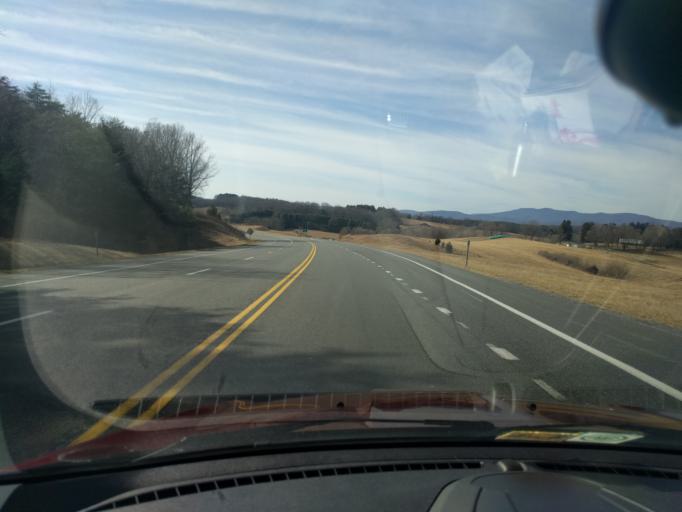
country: US
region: Virginia
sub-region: City of Staunton
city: Staunton
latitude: 38.1843
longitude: -79.0910
